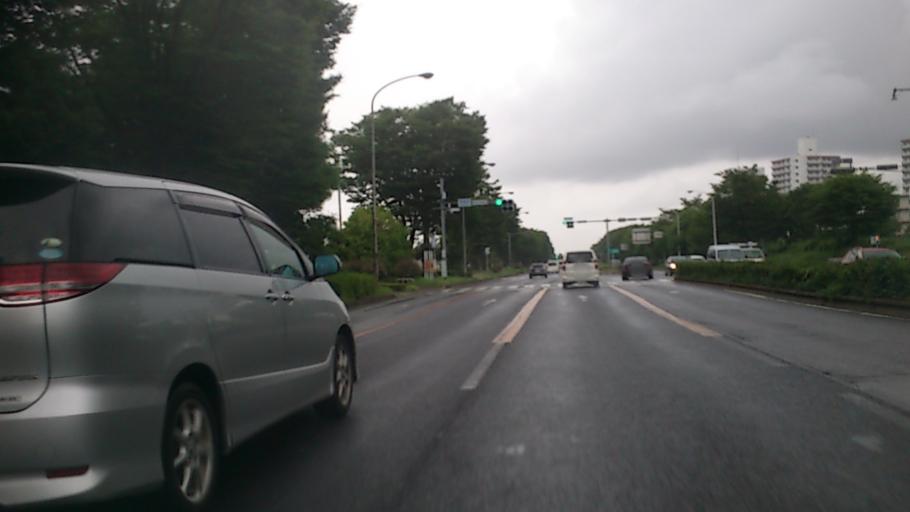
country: JP
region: Ibaraki
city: Naka
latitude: 36.0800
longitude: 140.1081
